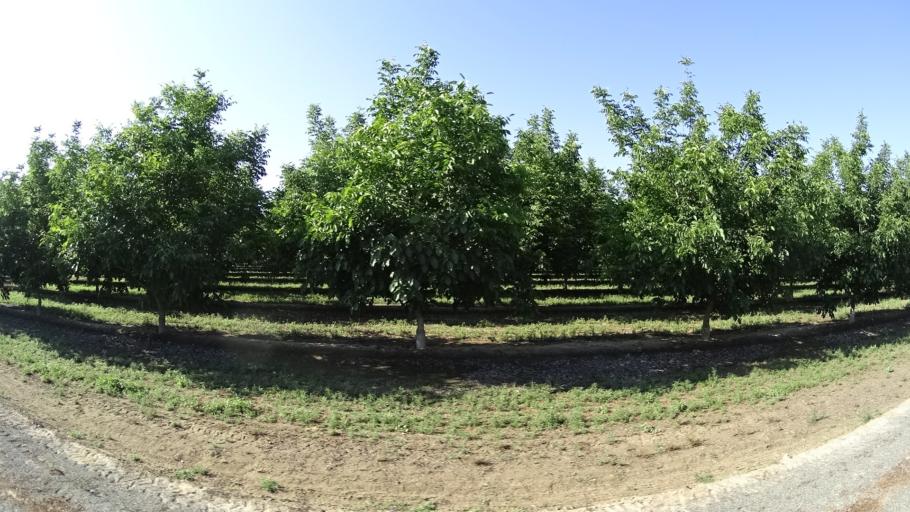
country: US
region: California
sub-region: Kings County
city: Lucerne
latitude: 36.3862
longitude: -119.7054
